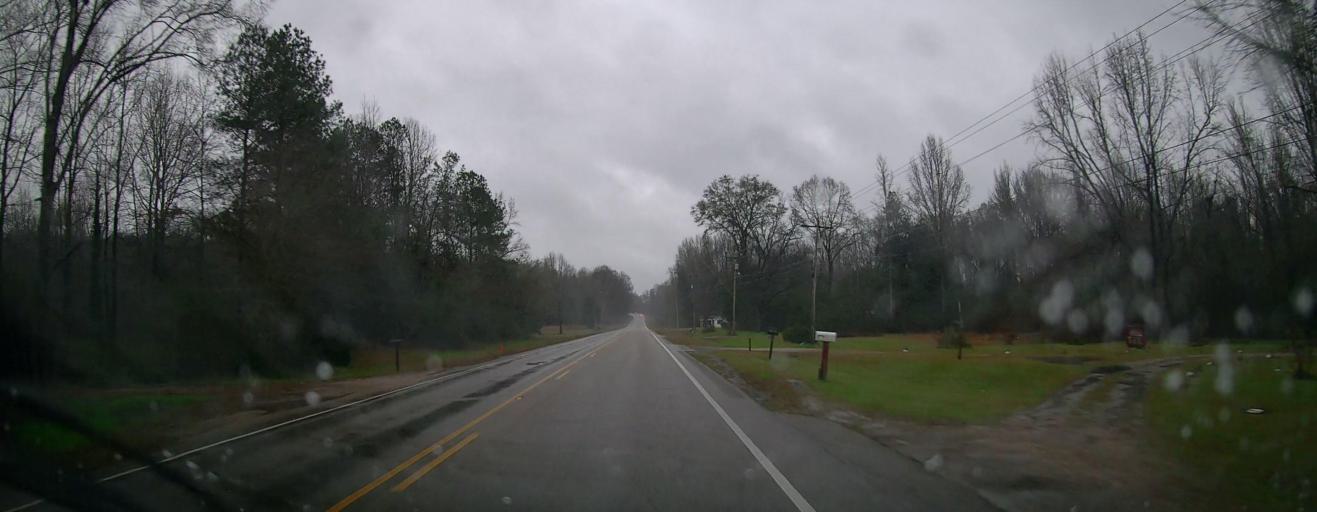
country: US
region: Alabama
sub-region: Autauga County
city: Prattville
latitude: 32.5051
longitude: -86.5857
